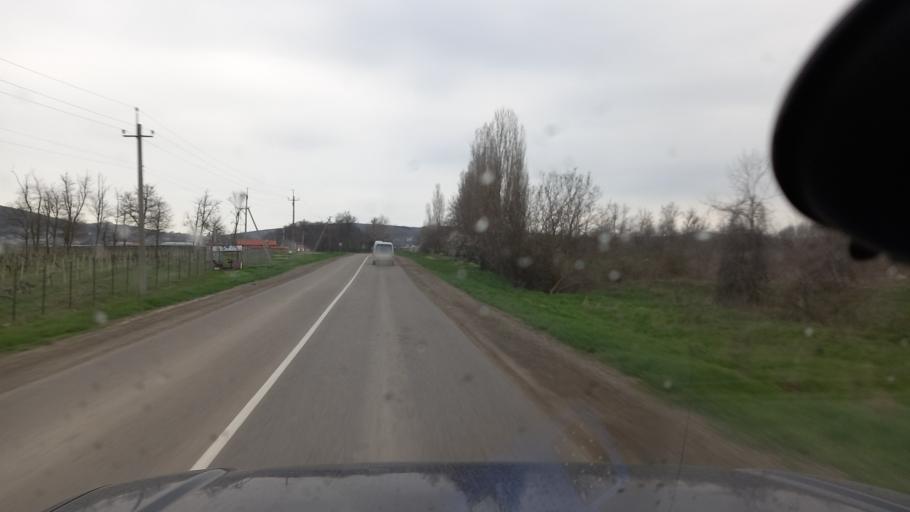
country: RU
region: Krasnodarskiy
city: Anapskaya
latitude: 44.8717
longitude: 37.4443
